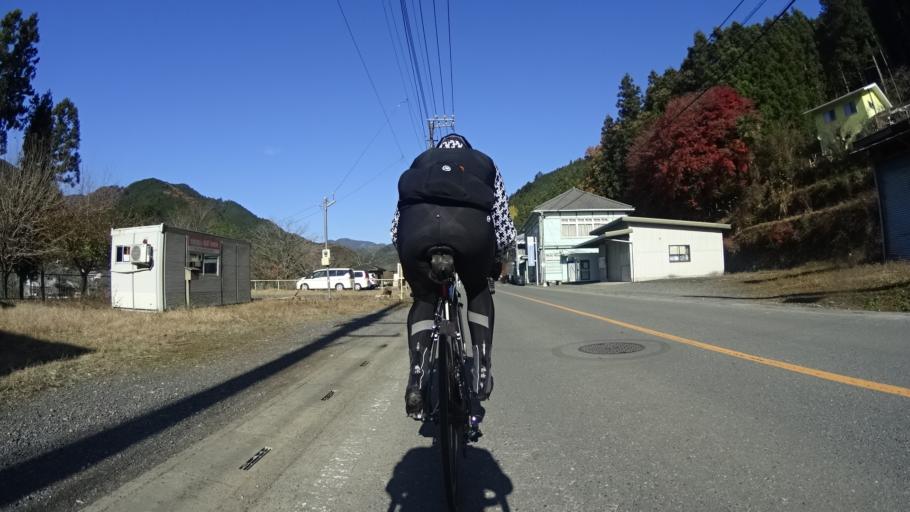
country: JP
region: Tokyo
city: Ome
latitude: 35.8836
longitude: 139.1834
